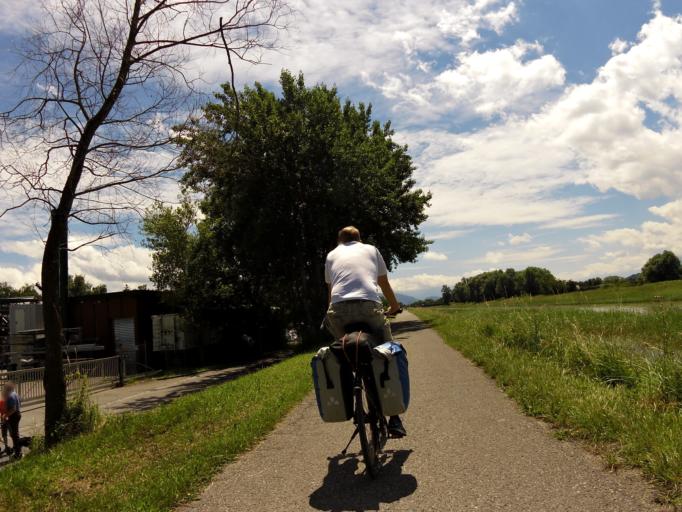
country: AT
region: Vorarlberg
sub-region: Politischer Bezirk Bregenz
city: Hard
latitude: 47.4839
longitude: 9.6752
